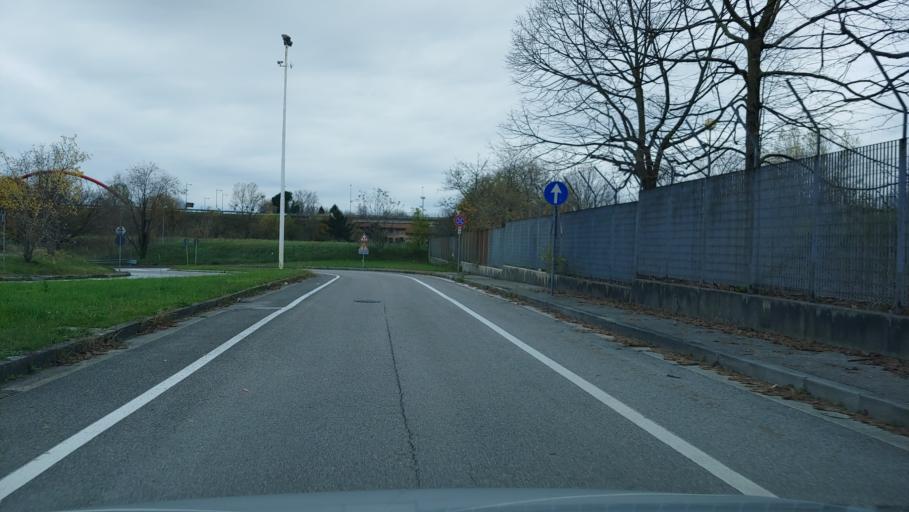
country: SI
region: Sempeter-Vrtojba
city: Vrtojba
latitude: 45.9203
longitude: 13.6172
